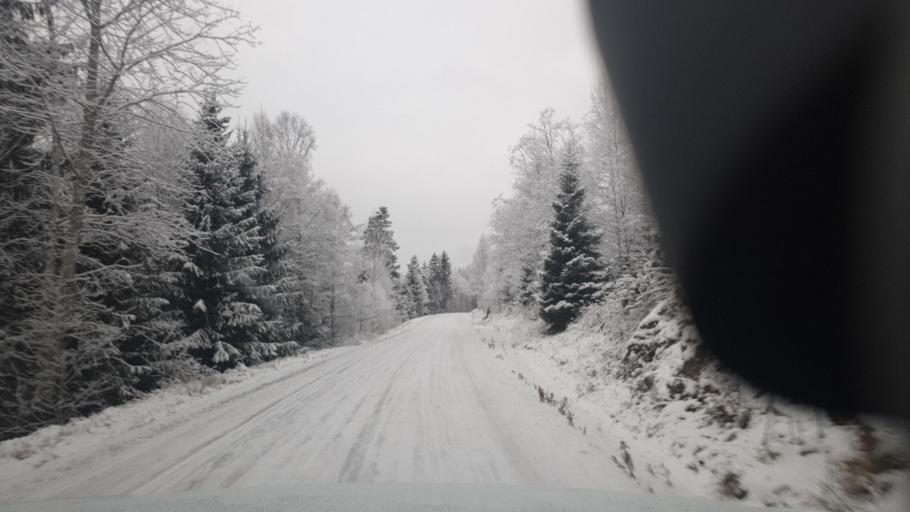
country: NO
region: Ostfold
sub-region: Romskog
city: Romskog
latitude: 59.8347
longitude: 11.9838
